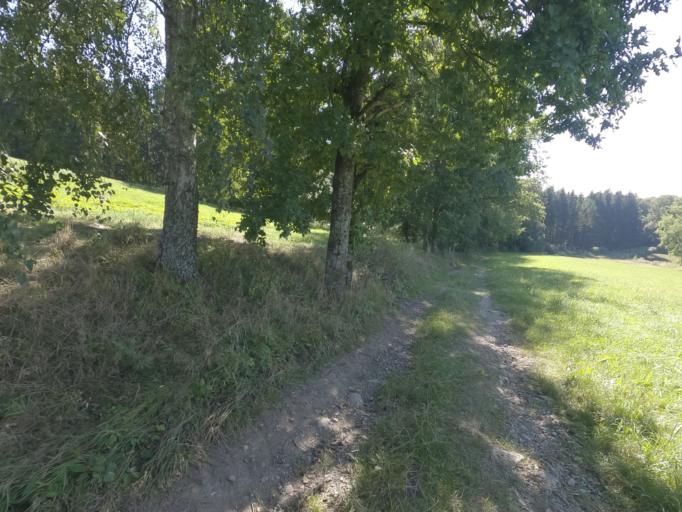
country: DE
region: Bavaria
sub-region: Lower Bavaria
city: Schaufling
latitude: 48.8318
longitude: 13.0242
